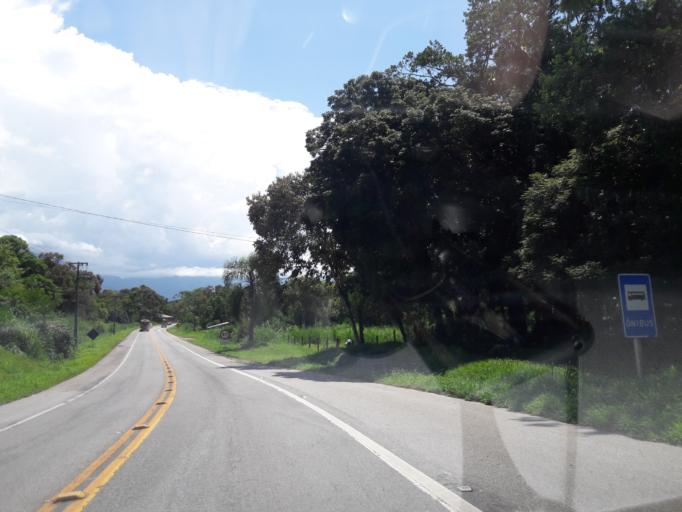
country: BR
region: Parana
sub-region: Antonina
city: Antonina
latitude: -25.5098
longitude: -48.8110
